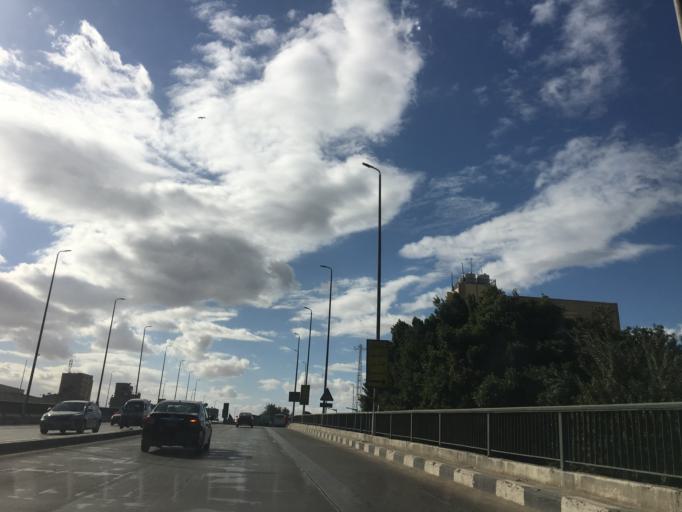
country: EG
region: Al Jizah
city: Al Jizah
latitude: 30.0277
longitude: 31.2023
